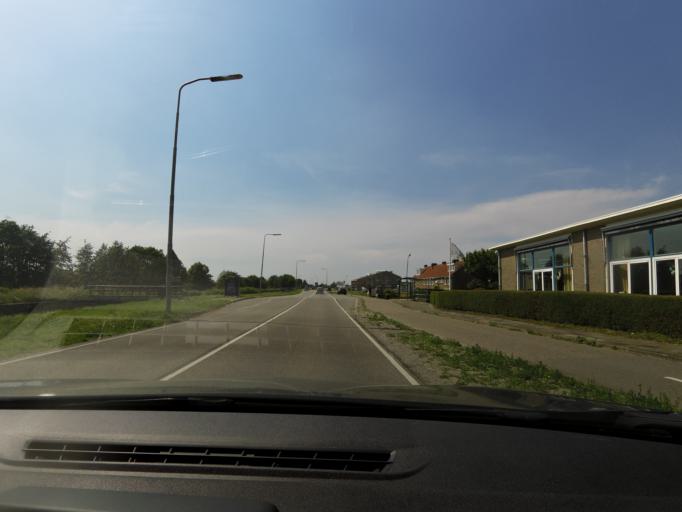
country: NL
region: South Holland
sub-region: Gemeente Lansingerland
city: Berkel en Rodenrijs
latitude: 51.9917
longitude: 4.4719
